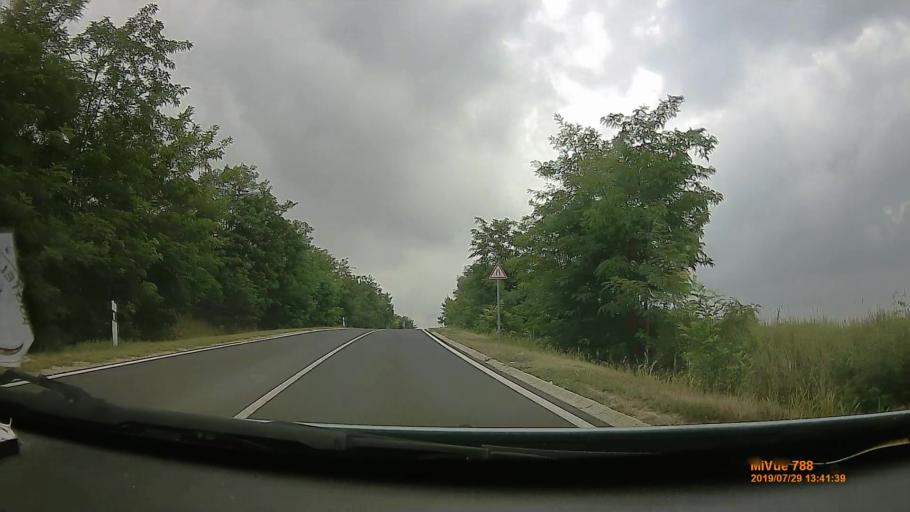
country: HU
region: Somogy
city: Balatonfoldvar
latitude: 46.8135
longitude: 17.9225
